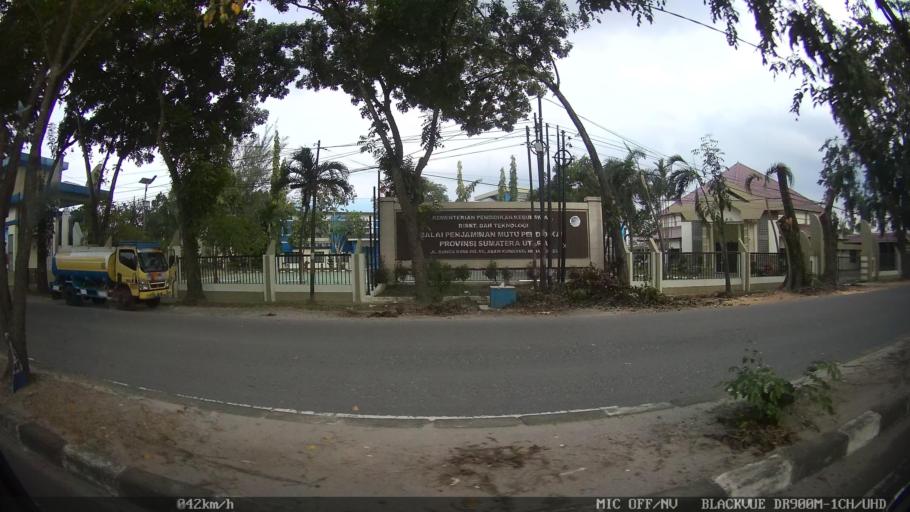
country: ID
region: North Sumatra
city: Sunggal
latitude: 3.5536
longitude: 98.6121
